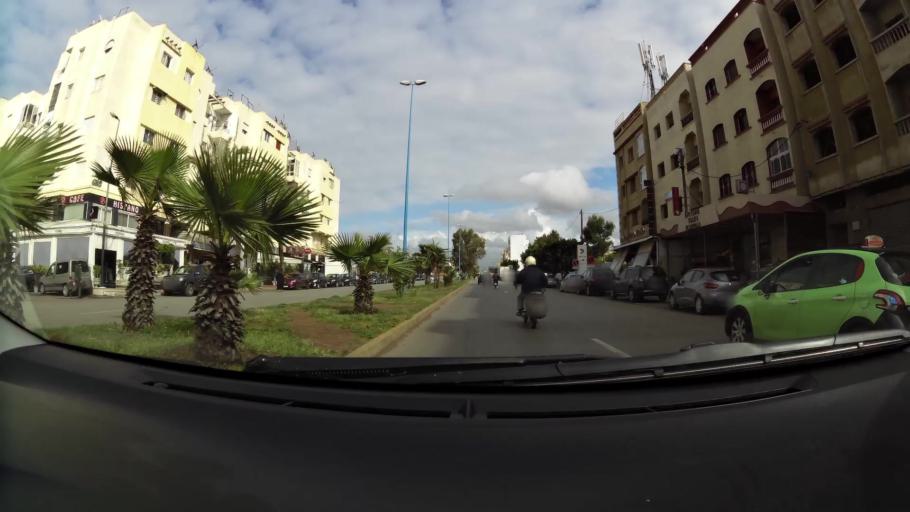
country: MA
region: Grand Casablanca
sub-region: Mohammedia
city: Mohammedia
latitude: 33.6934
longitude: -7.3770
